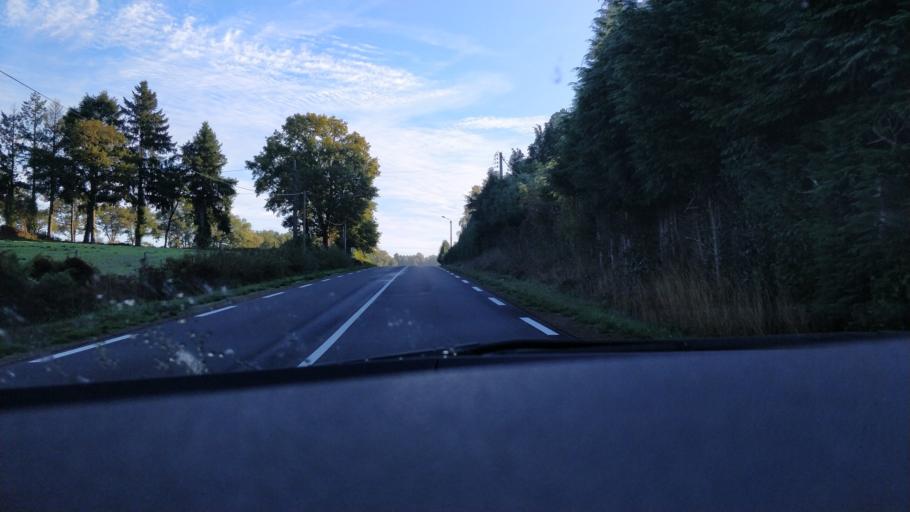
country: FR
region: Limousin
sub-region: Departement de la Haute-Vienne
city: Sauviat-sur-Vige
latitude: 45.9137
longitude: 1.6220
